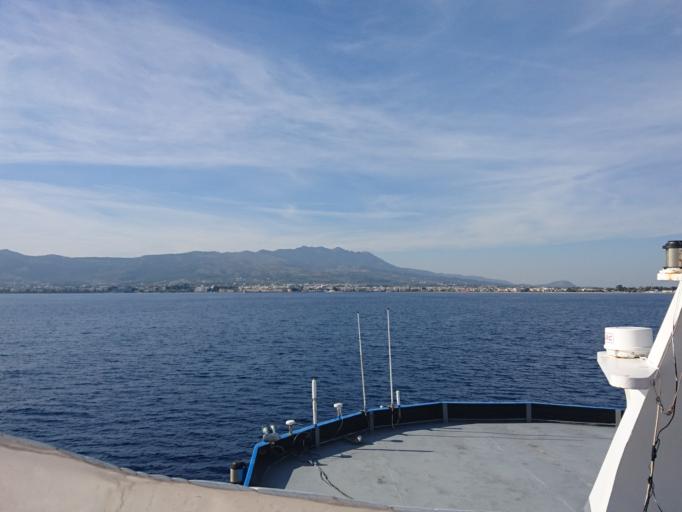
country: GR
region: South Aegean
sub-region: Nomos Dodekanisou
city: Kos
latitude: 36.9104
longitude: 27.3024
